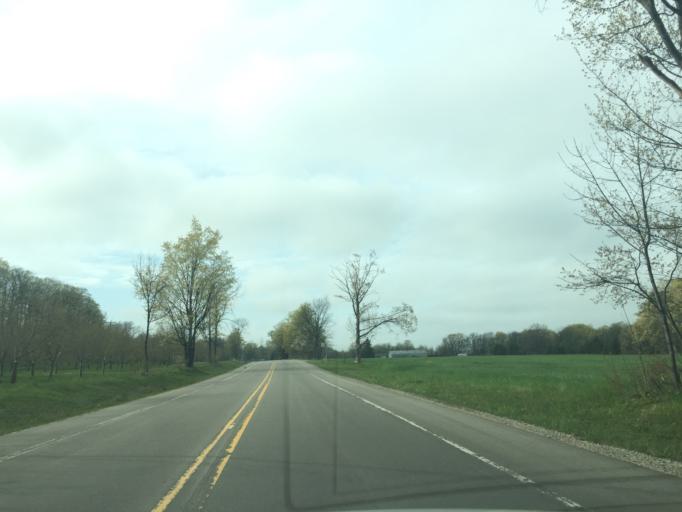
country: US
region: Michigan
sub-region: Leelanau County
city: Leland
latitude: 45.0718
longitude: -85.5881
